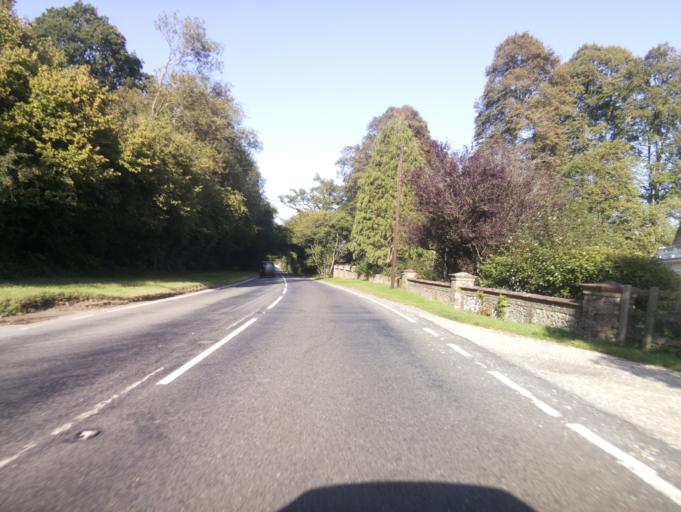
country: GB
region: England
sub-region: Hampshire
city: Four Marks
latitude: 51.0642
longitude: -1.0241
